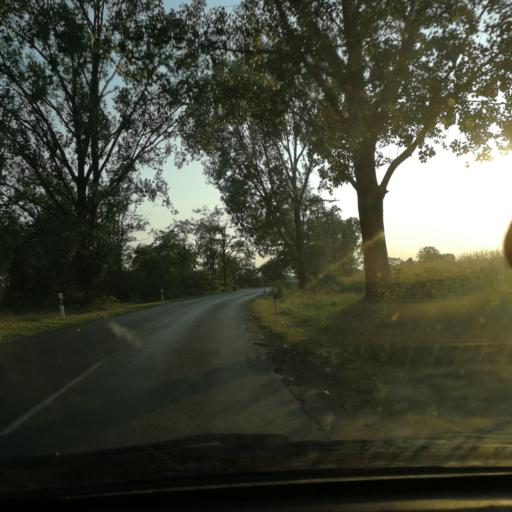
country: HU
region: Bacs-Kiskun
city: Kiskunhalas
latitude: 46.4292
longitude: 19.5279
